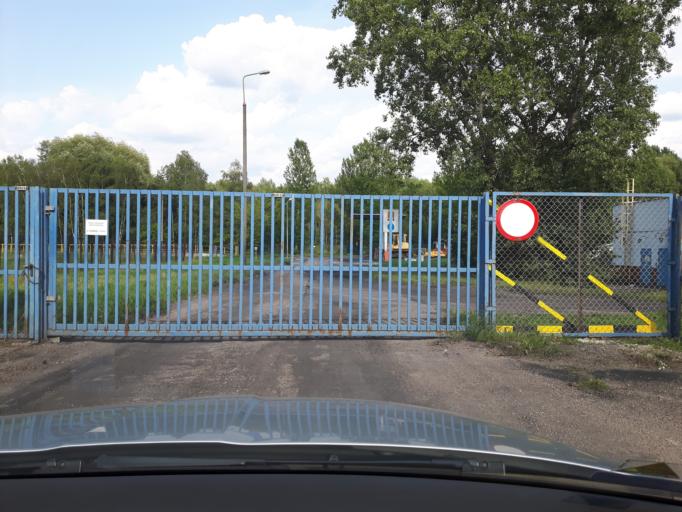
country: PL
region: Masovian Voivodeship
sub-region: Warszawa
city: Rembertow
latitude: 52.2697
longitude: 21.1311
